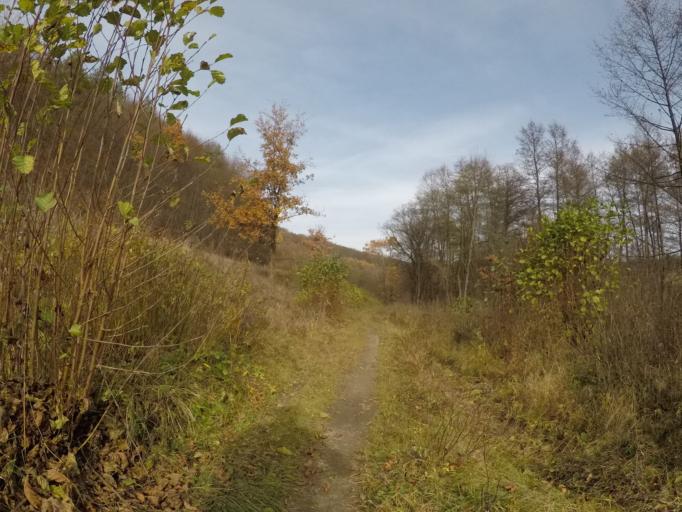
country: SK
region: Presovsky
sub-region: Okres Presov
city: Presov
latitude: 48.9551
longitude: 21.1914
